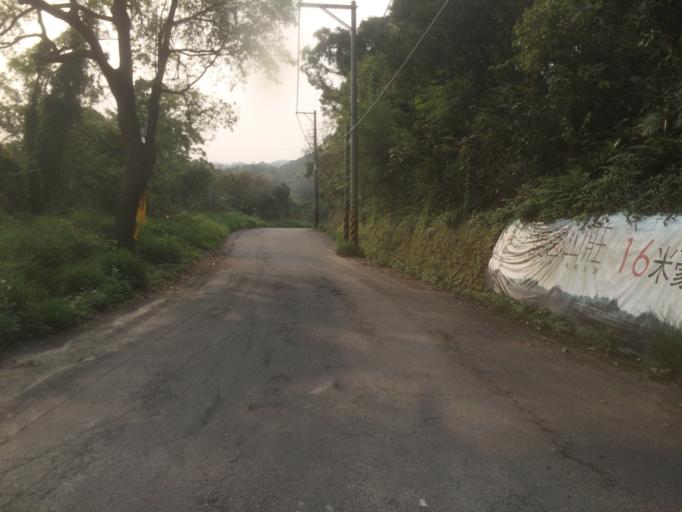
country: TW
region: Taiwan
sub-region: Hsinchu
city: Hsinchu
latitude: 24.7618
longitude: 120.9774
